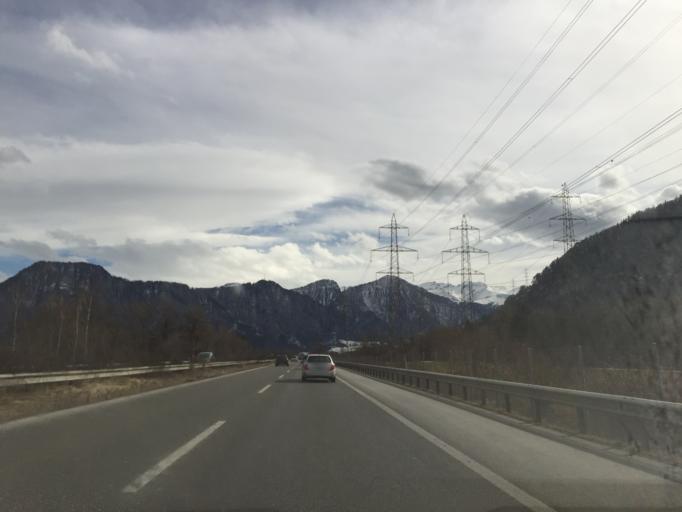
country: CH
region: Grisons
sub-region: Landquart District
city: Maienfeld
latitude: 46.9881
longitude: 9.5355
